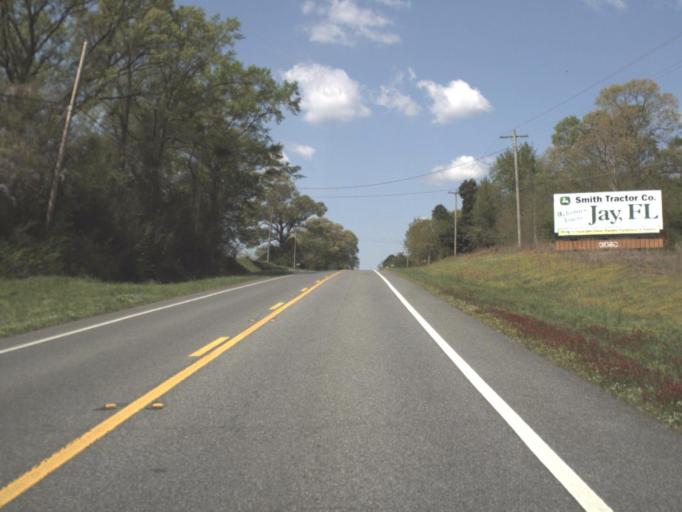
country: US
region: Alabama
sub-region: Escambia County
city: East Brewton
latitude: 30.9520
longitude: -87.1076
